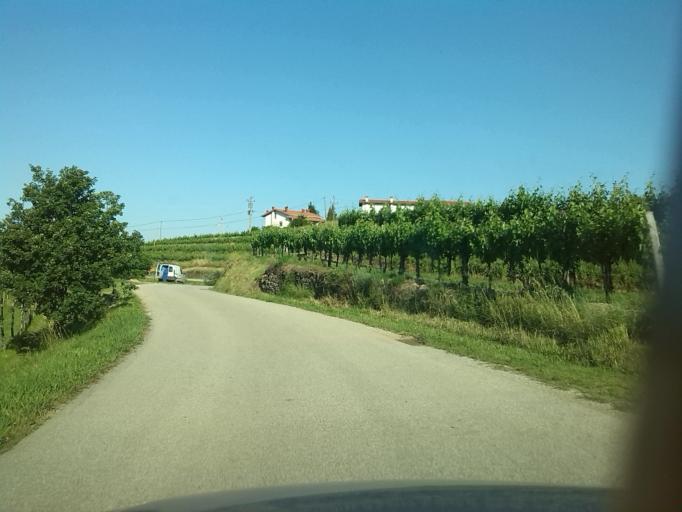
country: SI
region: Brda
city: Dobrovo
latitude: 45.9830
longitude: 13.5076
